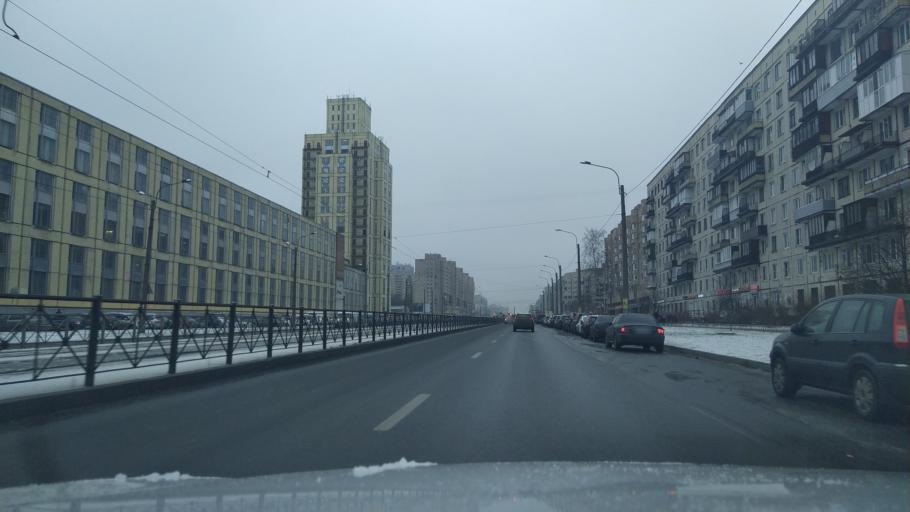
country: RU
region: St.-Petersburg
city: Grazhdanka
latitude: 60.0345
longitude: 30.4257
